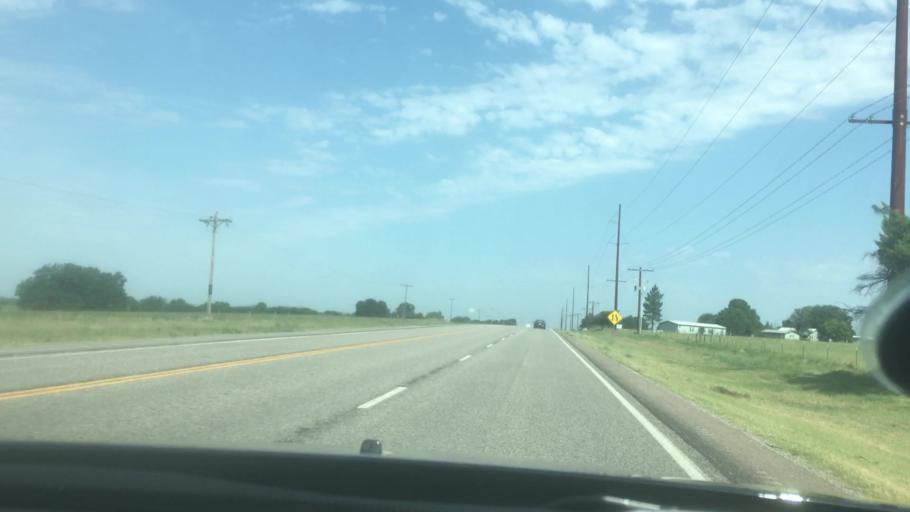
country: US
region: Oklahoma
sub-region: Seminole County
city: Konawa
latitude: 34.8499
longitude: -96.8098
